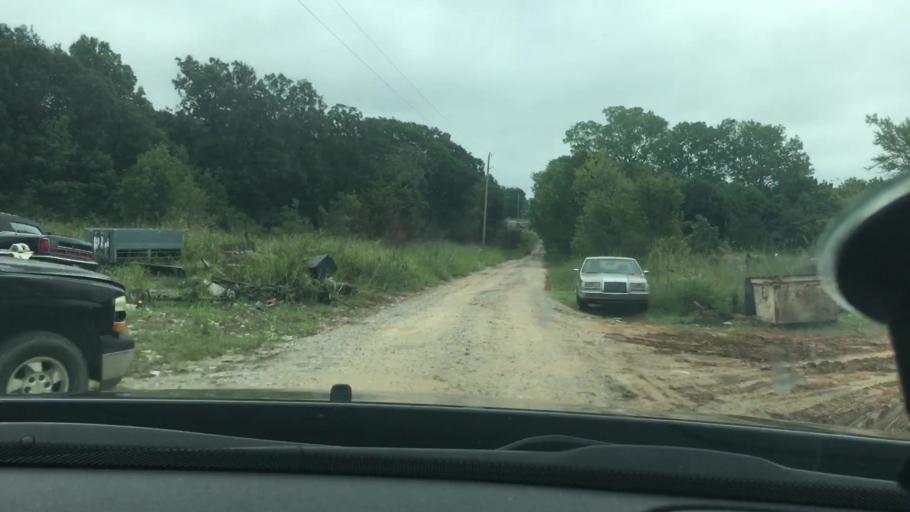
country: US
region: Oklahoma
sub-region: Pontotoc County
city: Ada
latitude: 34.8037
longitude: -96.7514
